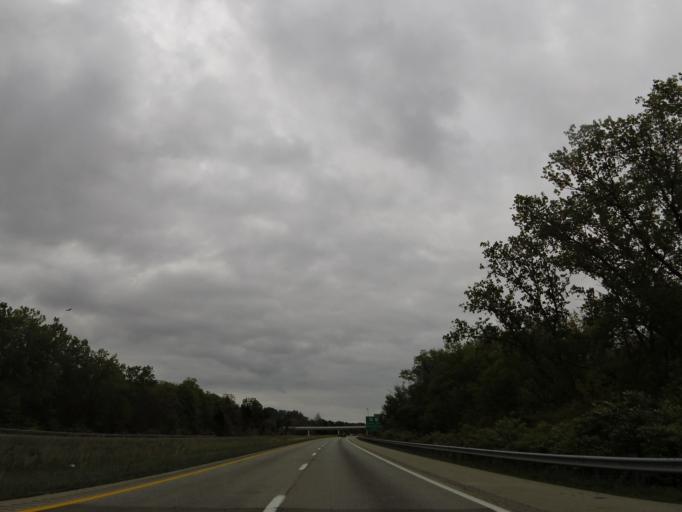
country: US
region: Ohio
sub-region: Franklin County
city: Grove City
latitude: 39.8239
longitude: -83.1600
